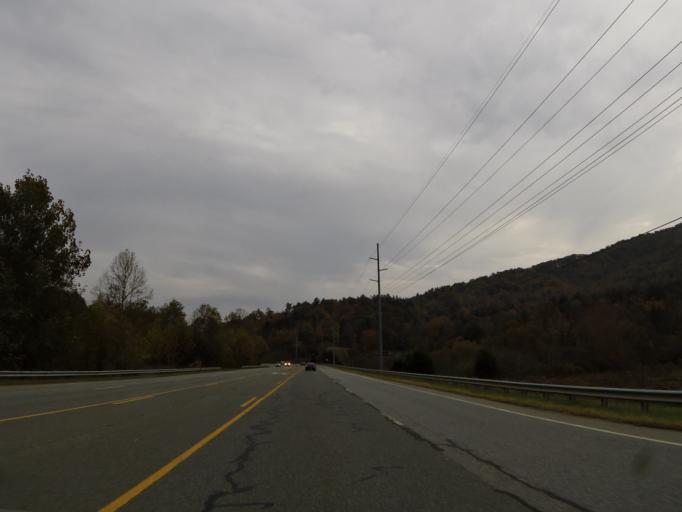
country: US
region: North Carolina
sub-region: Caldwell County
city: Lenoir
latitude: 36.0120
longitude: -81.5715
